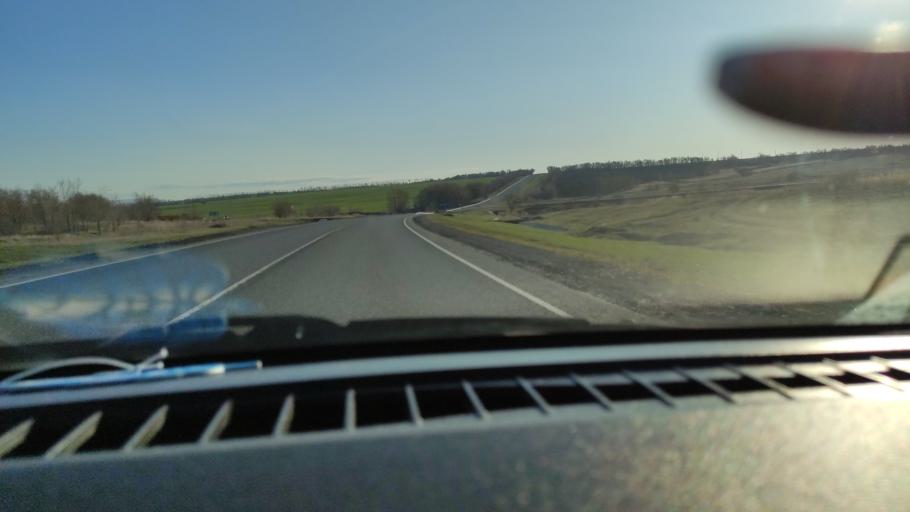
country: RU
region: Saratov
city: Balakovo
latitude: 52.1289
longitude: 47.7596
